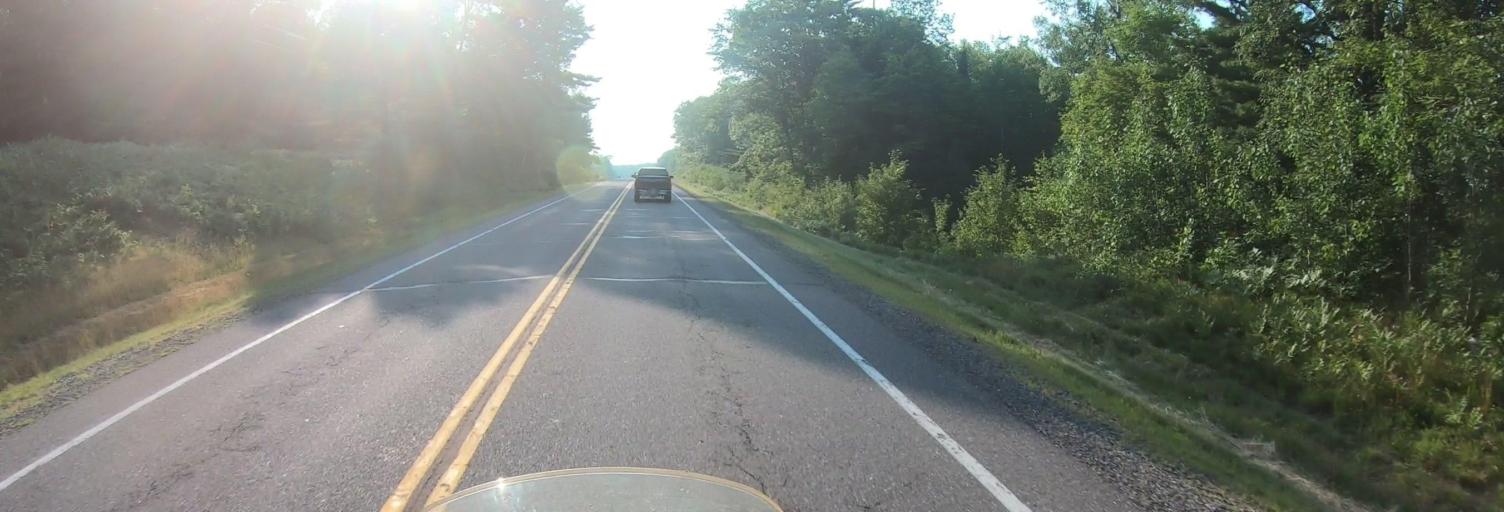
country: US
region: Wisconsin
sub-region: Sawyer County
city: Little Round Lake
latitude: 46.0649
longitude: -91.1621
